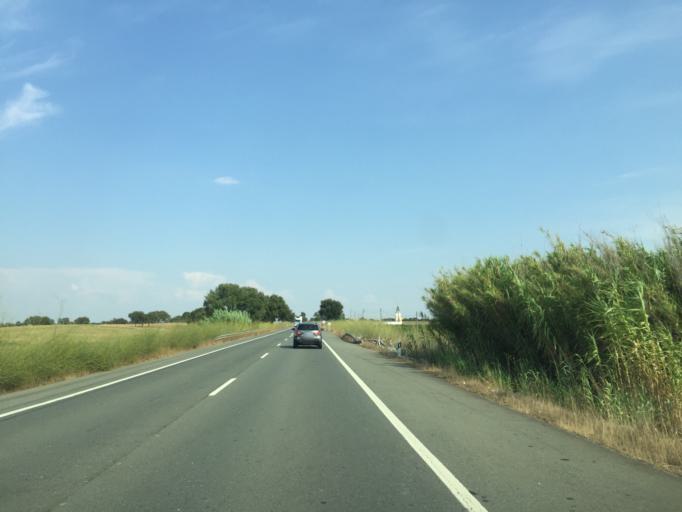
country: PT
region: Beja
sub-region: Aljustrel
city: Aljustrel
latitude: 37.9383
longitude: -8.3667
